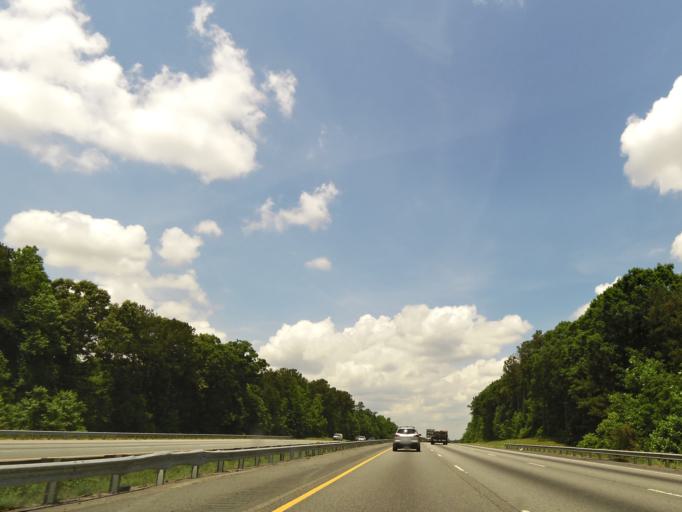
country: US
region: Georgia
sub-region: Henry County
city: Locust Grove
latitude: 33.3192
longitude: -84.1197
